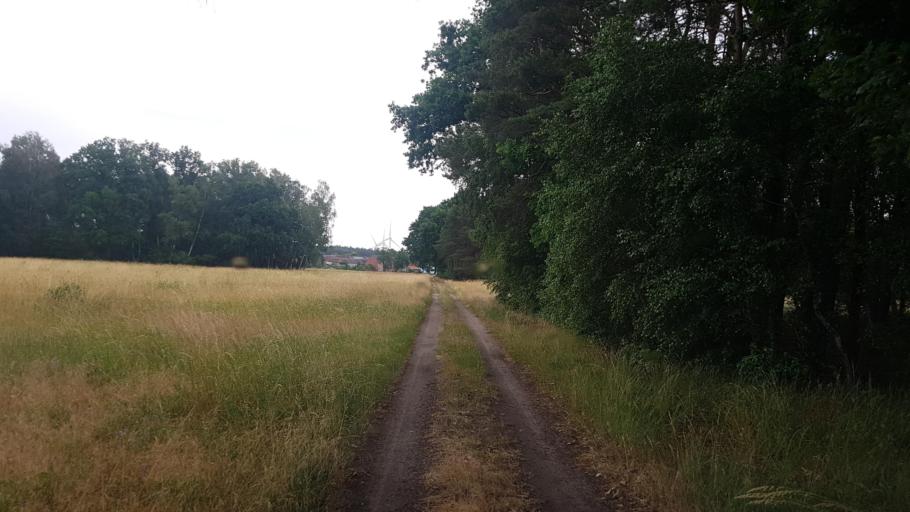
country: DE
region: Brandenburg
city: Schilda
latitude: 51.6406
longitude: 13.3867
